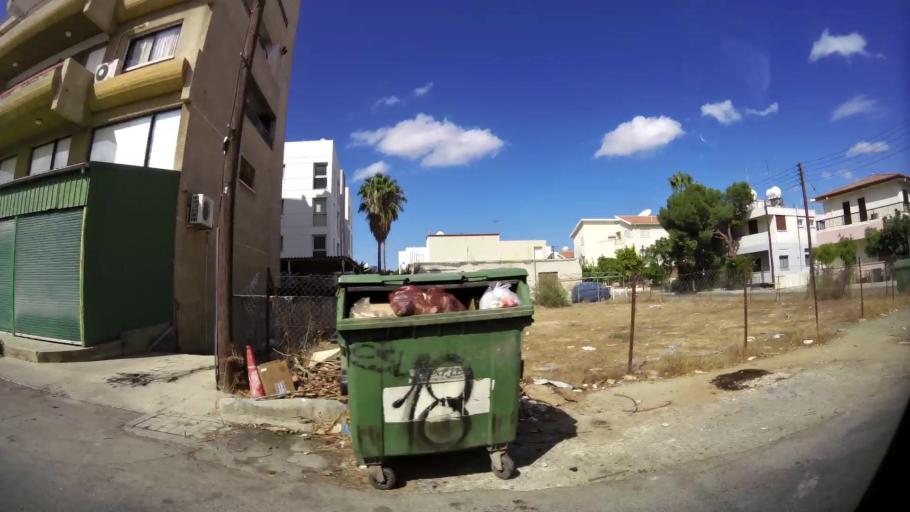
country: CY
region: Lefkosia
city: Nicosia
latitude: 35.1438
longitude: 33.3683
